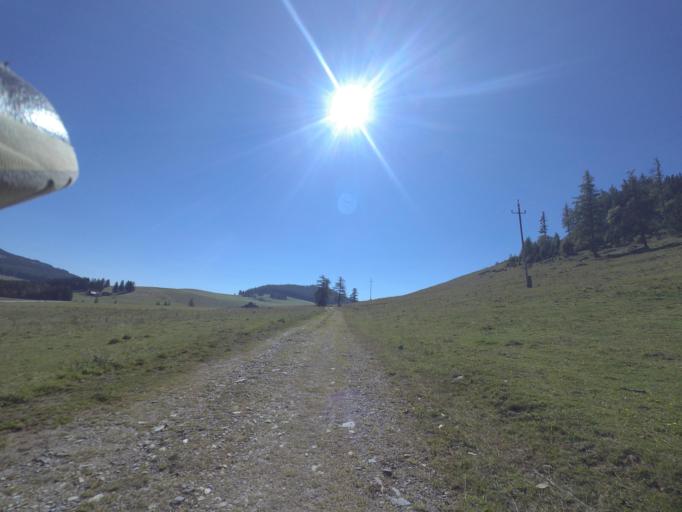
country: AT
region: Styria
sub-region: Politischer Bezirk Weiz
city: Passail
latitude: 47.3470
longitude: 15.4631
